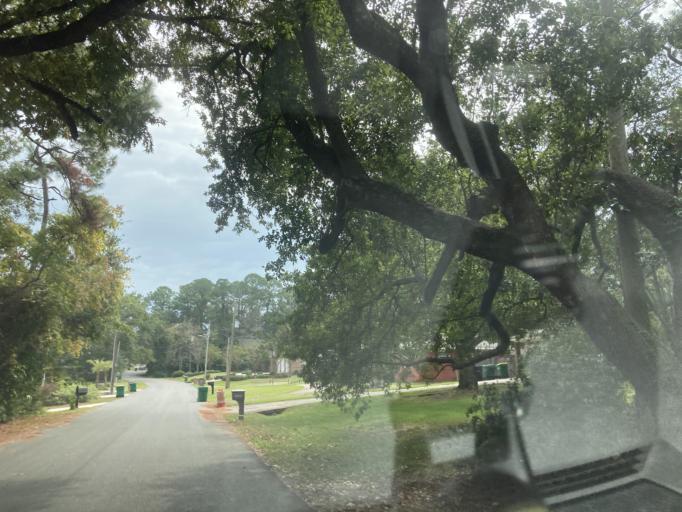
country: US
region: Mississippi
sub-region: Jackson County
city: Gulf Hills
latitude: 30.4350
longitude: -88.8434
